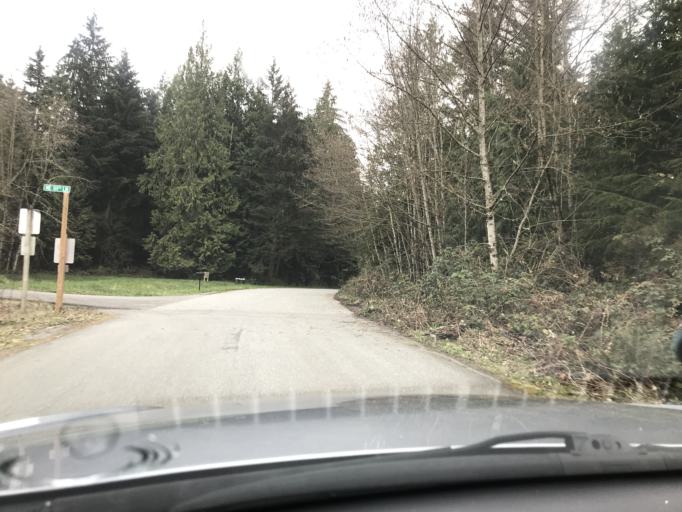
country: US
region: Washington
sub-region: King County
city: Union Hill-Novelty Hill
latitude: 47.6977
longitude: -122.0414
